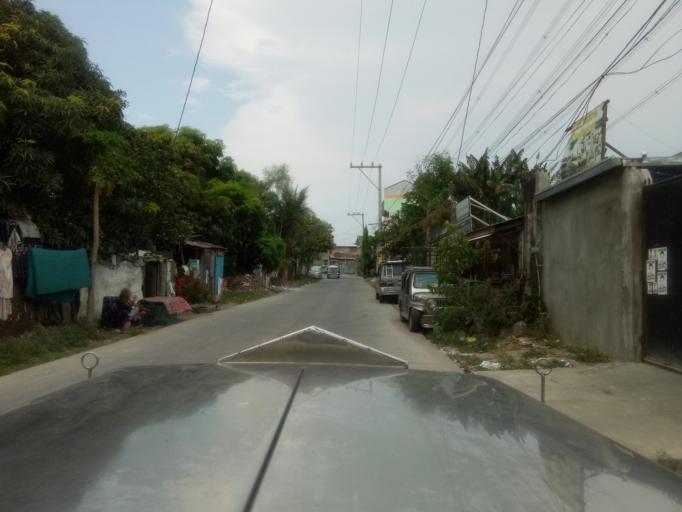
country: PH
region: Calabarzon
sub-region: Province of Cavite
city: Bulihan
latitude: 14.3129
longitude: 120.9751
